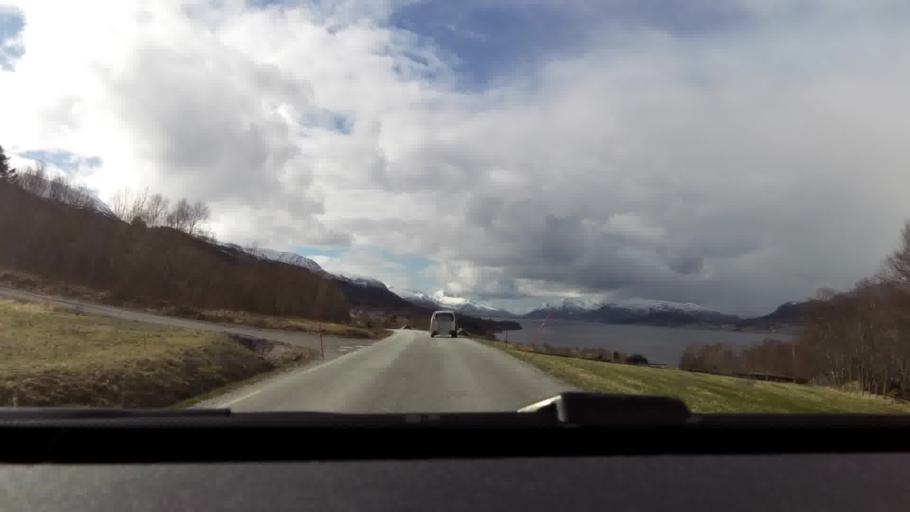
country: NO
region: More og Romsdal
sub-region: Gjemnes
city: Batnfjordsora
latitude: 62.9633
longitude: 7.6793
